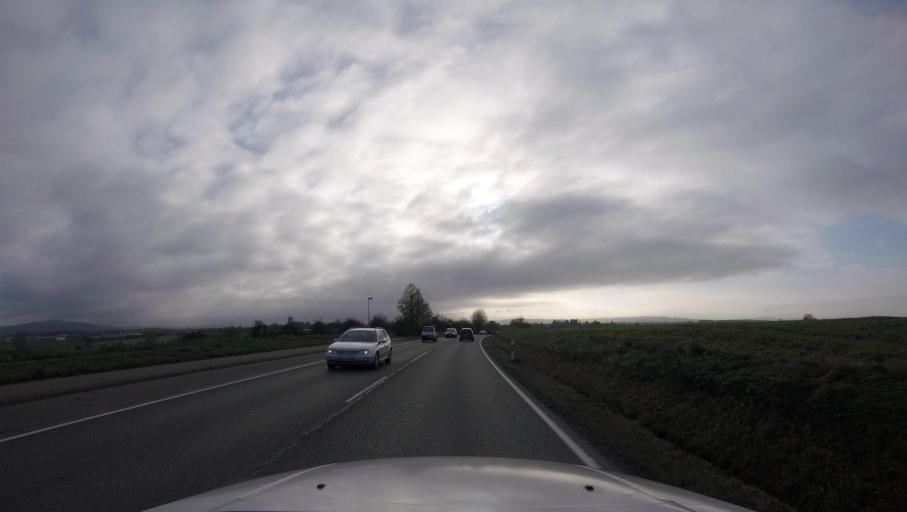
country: DE
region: Baden-Wuerttemberg
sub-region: Regierungsbezirk Stuttgart
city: Aspach
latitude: 48.9591
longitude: 9.4079
